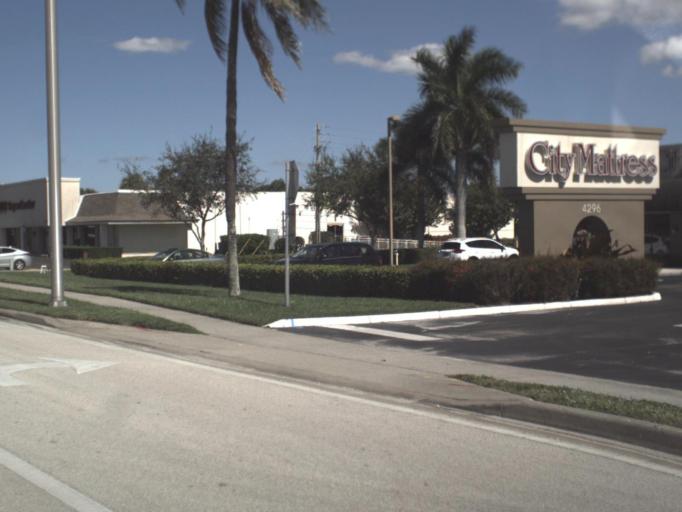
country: US
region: Florida
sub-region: Collier County
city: Pine Ridge
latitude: 26.1987
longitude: -81.8001
